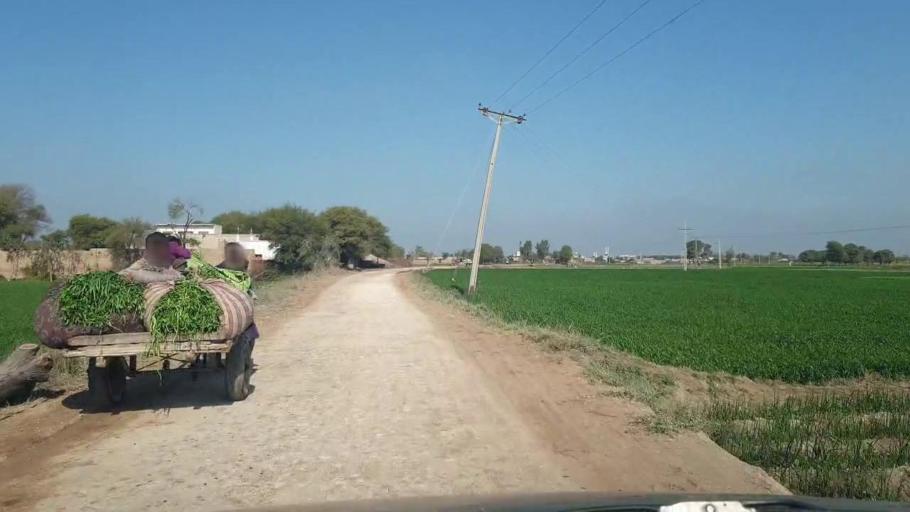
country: PK
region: Sindh
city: Bhit Shah
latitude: 25.8893
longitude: 68.5264
